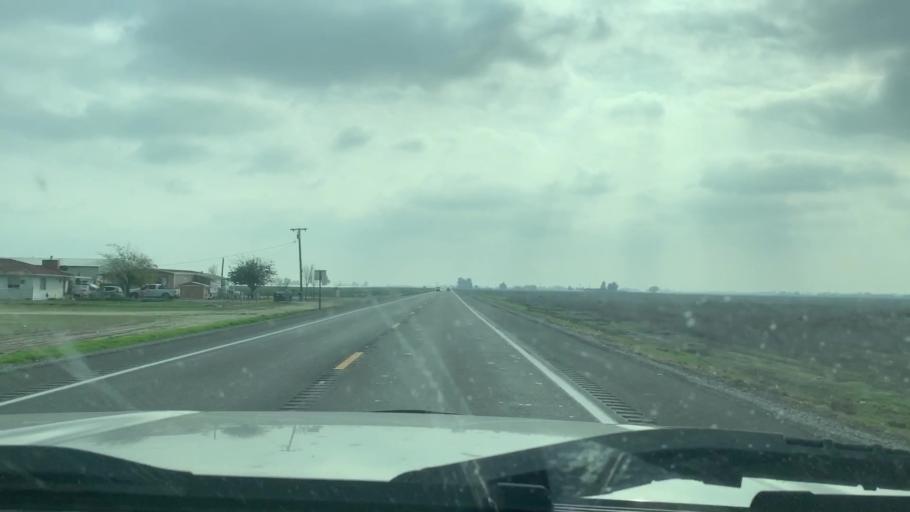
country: US
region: California
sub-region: Kings County
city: Stratford
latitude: 36.2250
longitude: -119.8162
